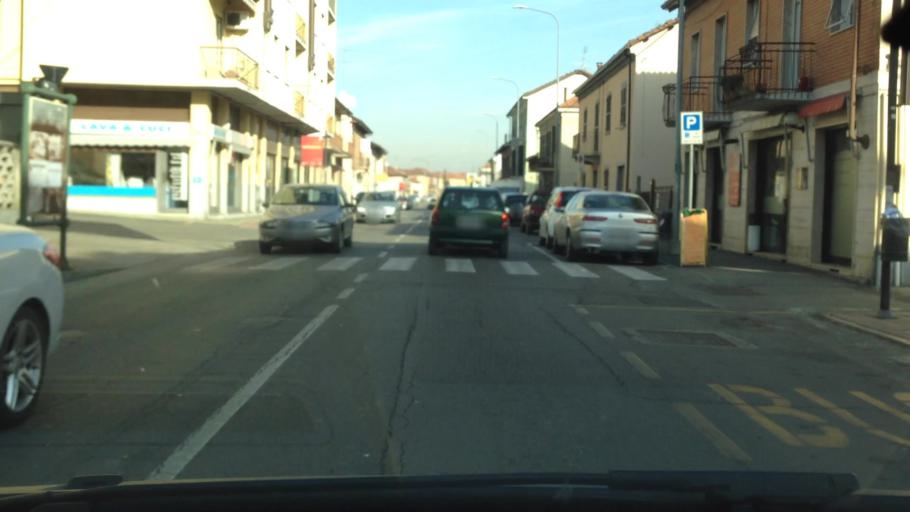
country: IT
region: Piedmont
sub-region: Provincia di Asti
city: Asti
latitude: 44.9099
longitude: 8.2195
